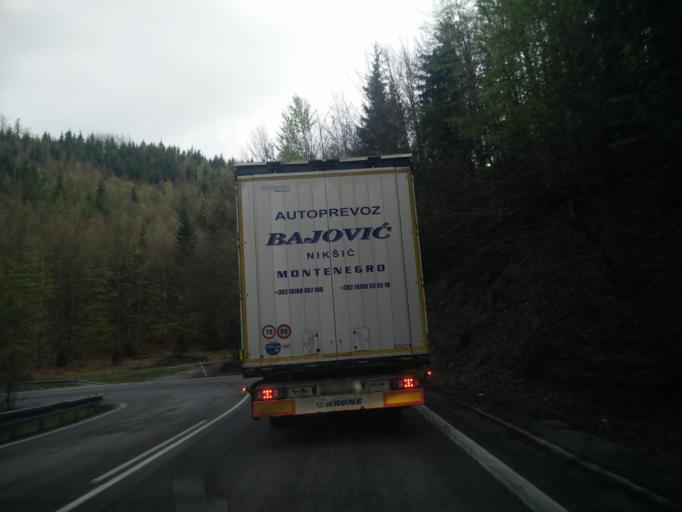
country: SK
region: Banskobystricky
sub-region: Okres Ziar nad Hronom
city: Kremnica
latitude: 48.8319
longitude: 19.0122
